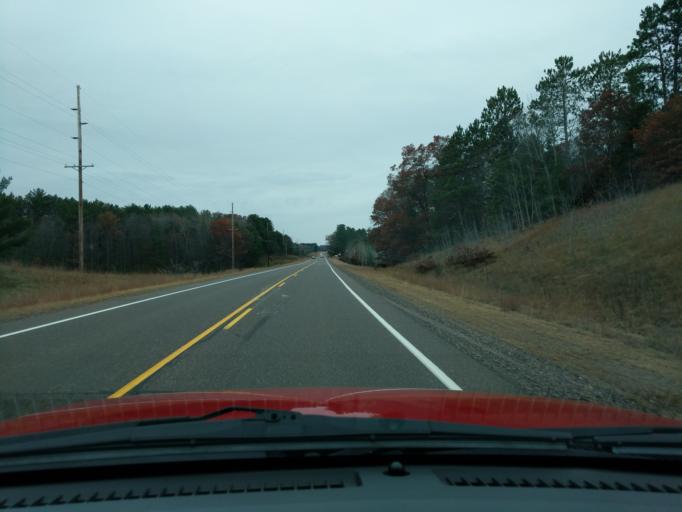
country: US
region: Wisconsin
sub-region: Burnett County
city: Siren
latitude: 45.8096
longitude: -92.2208
